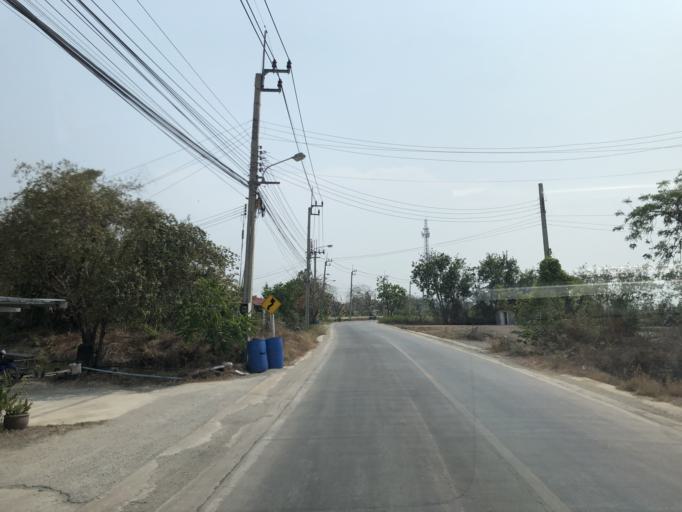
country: TH
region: Samut Prakan
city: Bang Bo
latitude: 13.5358
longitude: 100.8726
